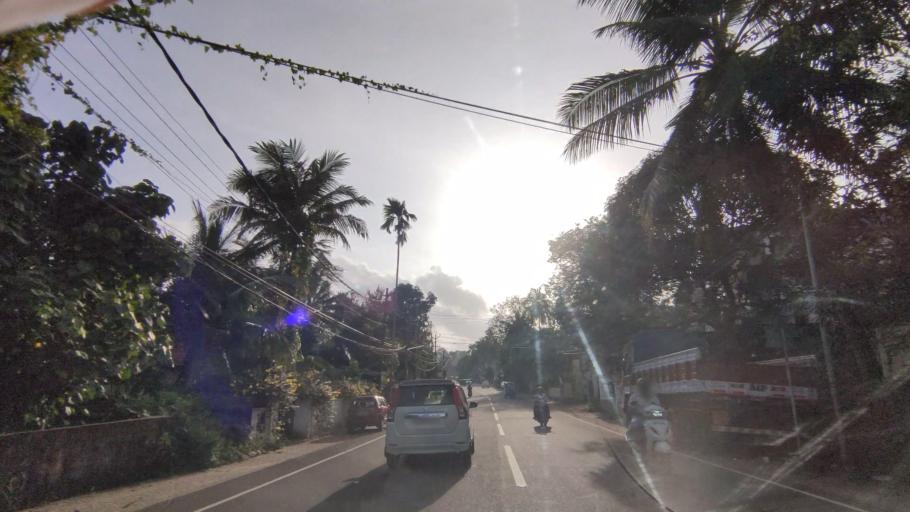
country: IN
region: Kerala
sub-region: Kottayam
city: Kottayam
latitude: 9.5944
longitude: 76.5048
